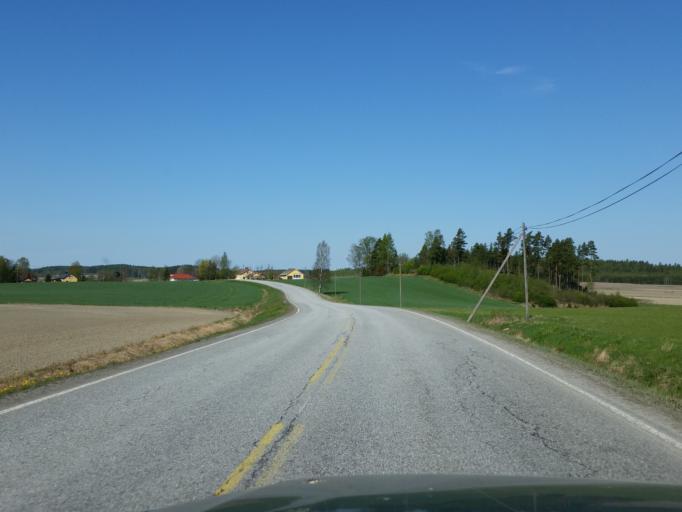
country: FI
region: Uusimaa
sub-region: Helsinki
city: Lohja
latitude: 60.1769
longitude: 24.0864
